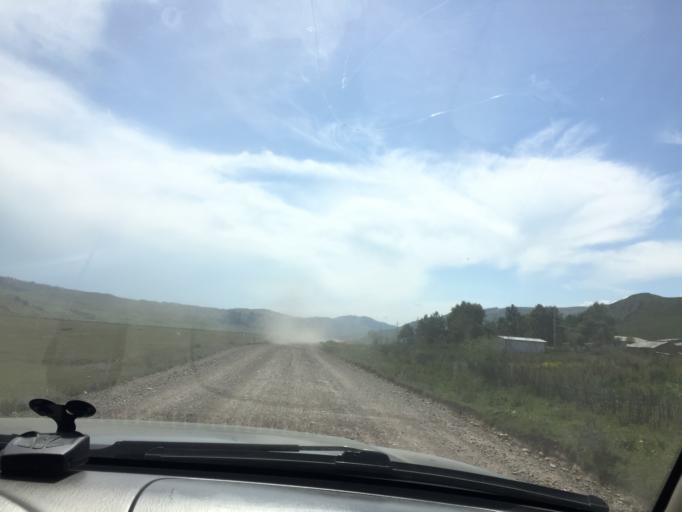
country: KZ
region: Almaty Oblysy
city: Kegen
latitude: 42.7525
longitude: 78.9961
